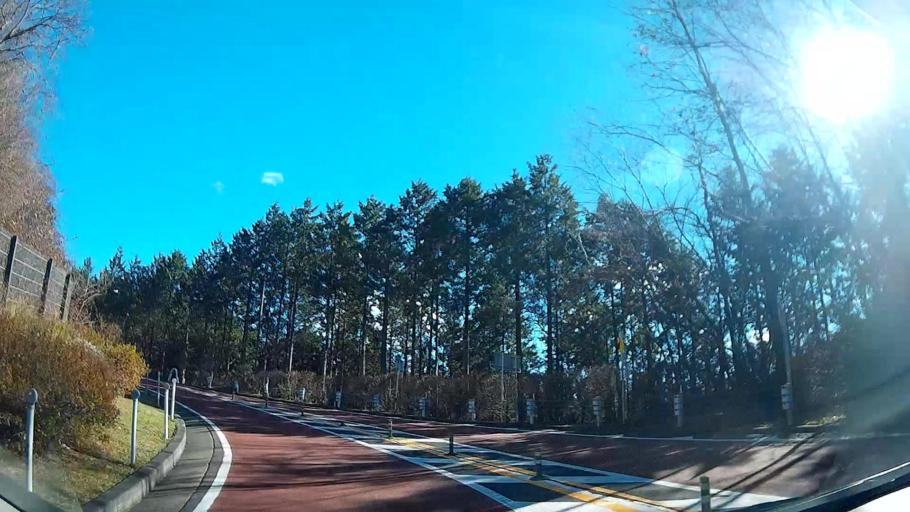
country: JP
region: Yamanashi
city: Uenohara
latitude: 35.7372
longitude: 139.0416
